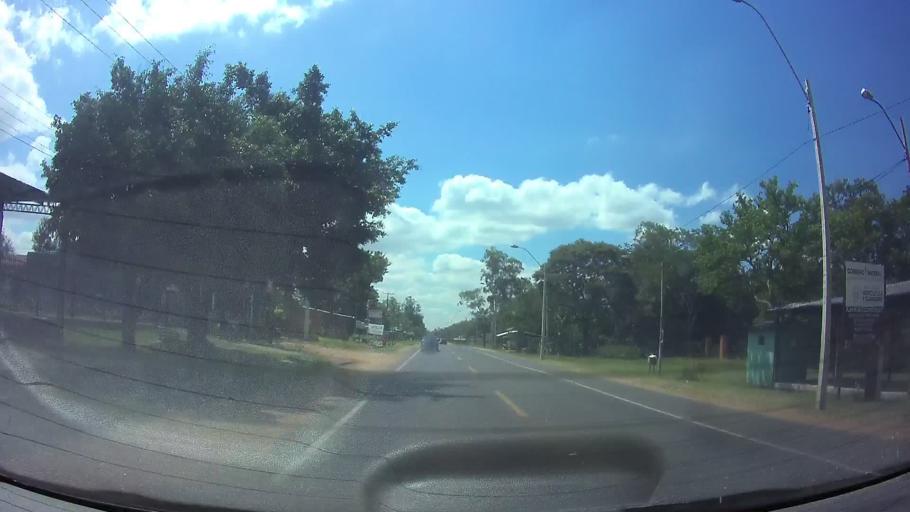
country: PY
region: Central
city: Aregua
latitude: -25.3332
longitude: -57.3557
